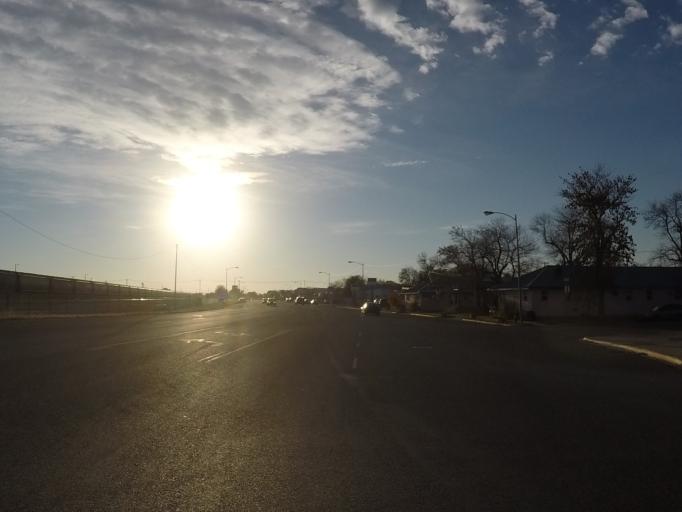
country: US
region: Montana
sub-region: Yellowstone County
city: Laurel
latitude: 45.6716
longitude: -108.7611
